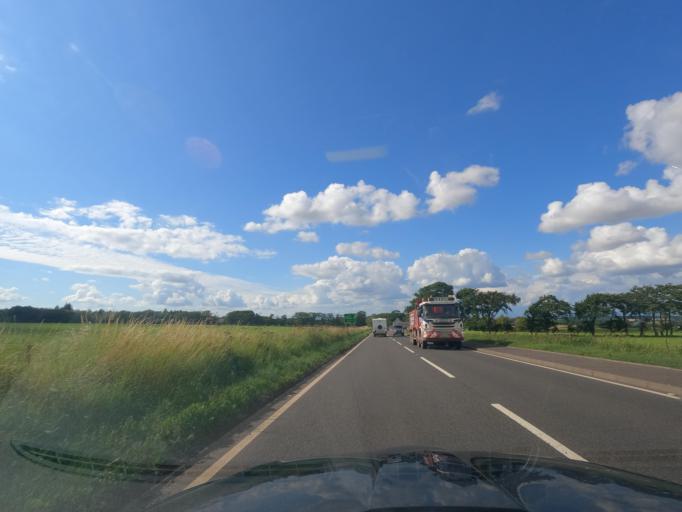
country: GB
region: Scotland
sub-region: East Lothian
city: Pencaitland
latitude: 55.8308
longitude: -2.8857
